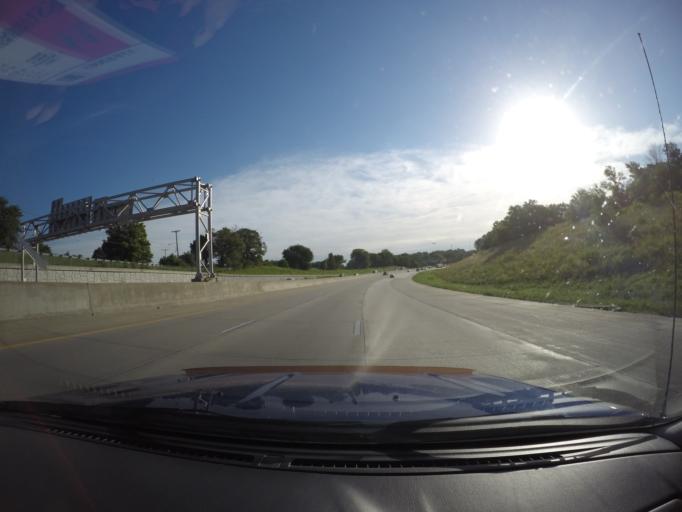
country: US
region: Kansas
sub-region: Wyandotte County
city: Kansas City
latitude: 39.1451
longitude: -94.6686
